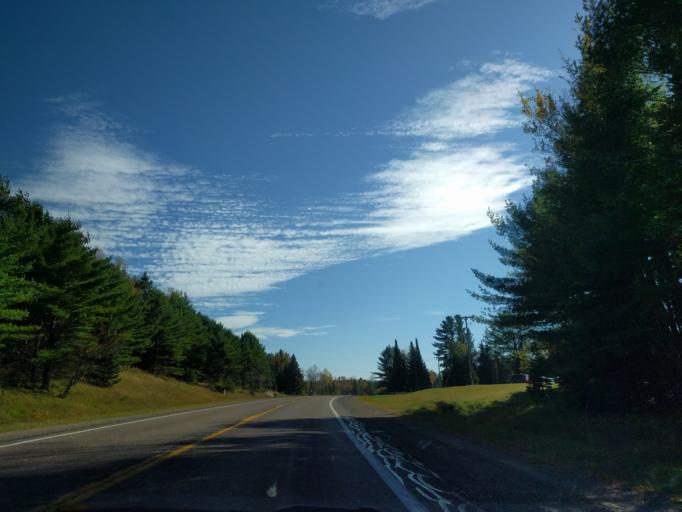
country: US
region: Michigan
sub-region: Marquette County
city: West Ishpeming
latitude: 46.3476
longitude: -87.9766
